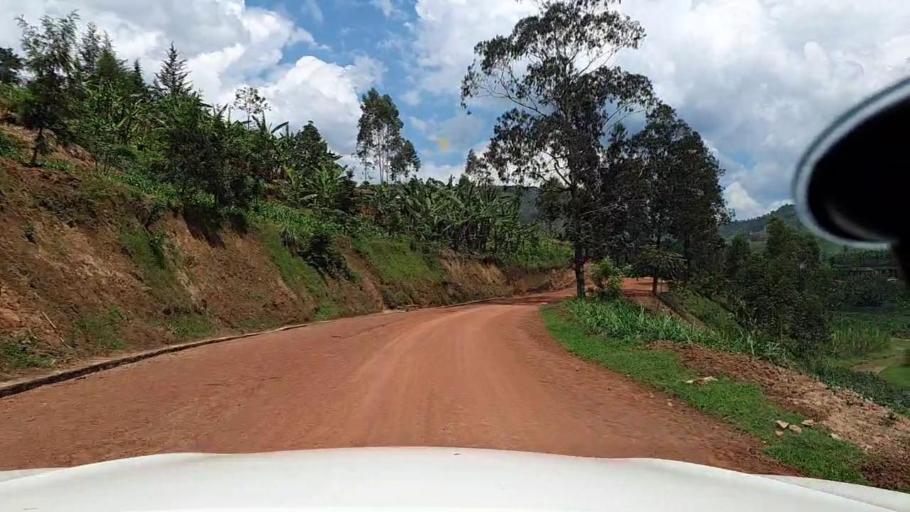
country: RW
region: Northern Province
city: Musanze
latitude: -1.6937
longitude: 29.8197
